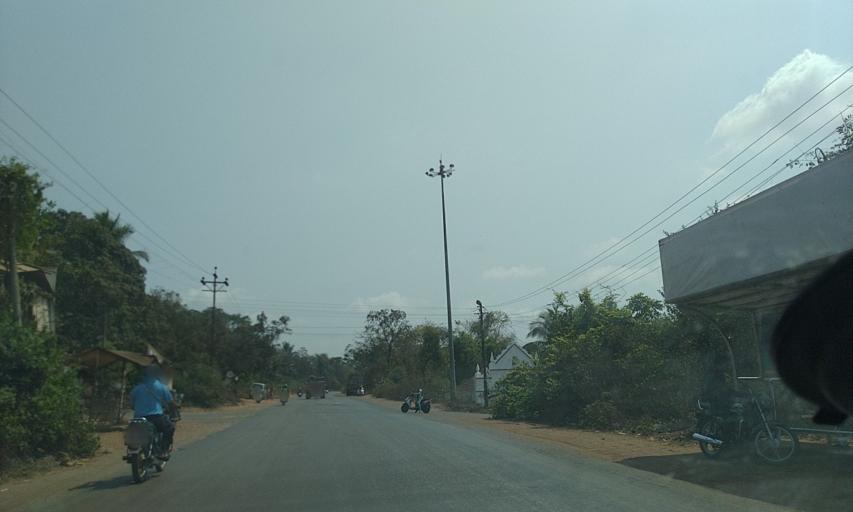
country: IN
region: Goa
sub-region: North Goa
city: Colovale
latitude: 15.6453
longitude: 73.8349
